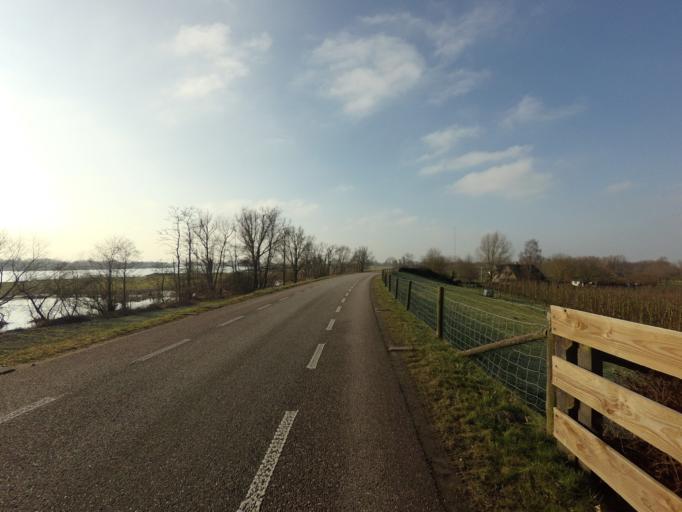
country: NL
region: Utrecht
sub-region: Gemeente Lopik
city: Lopik
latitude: 51.9658
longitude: 4.9488
